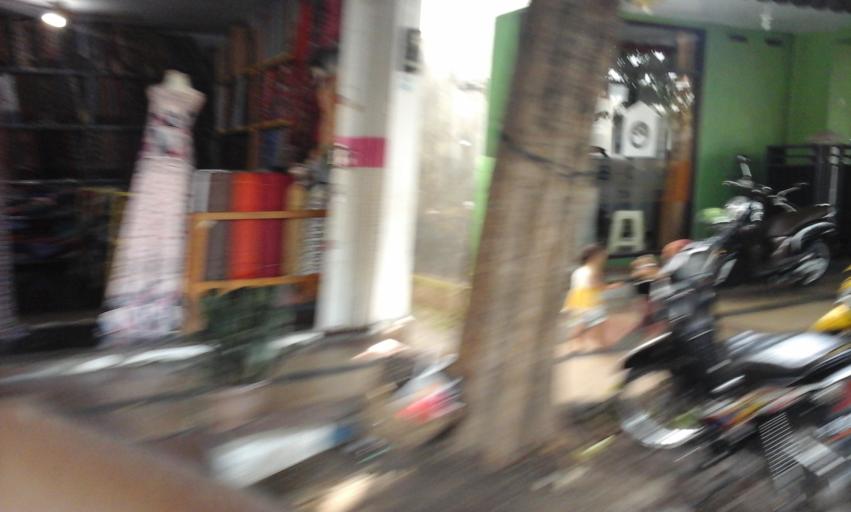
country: ID
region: East Java
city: Wirodayan
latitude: -8.2088
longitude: 114.3686
